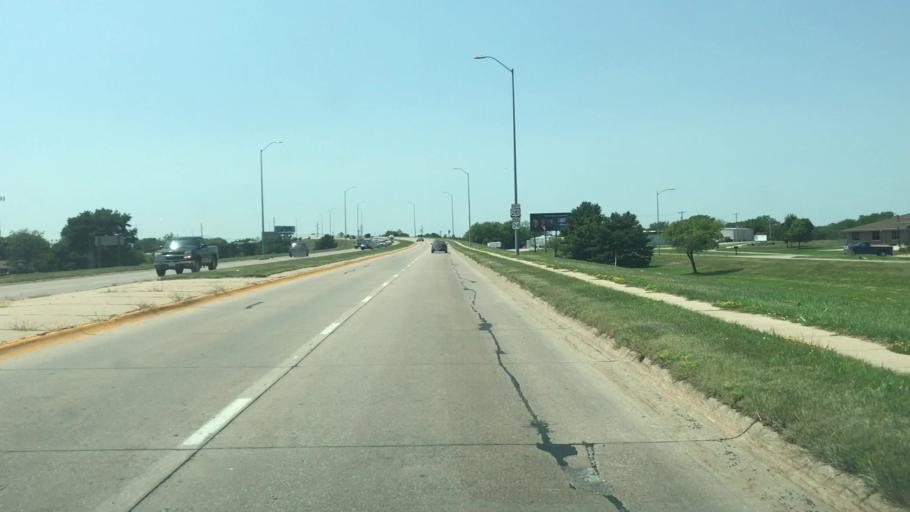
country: US
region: Nebraska
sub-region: Adams County
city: Hastings
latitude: 40.6085
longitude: -98.3873
